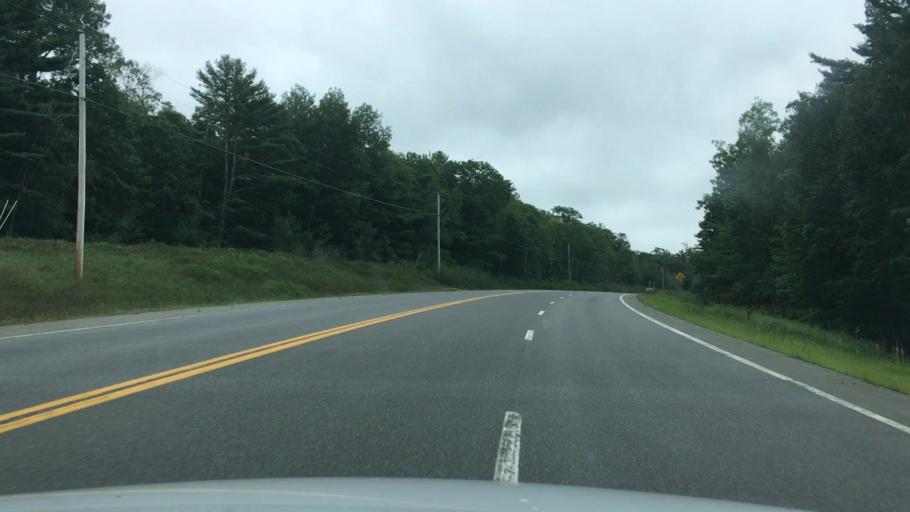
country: US
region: Maine
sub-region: Hancock County
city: Franklin
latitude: 44.8402
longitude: -68.1499
